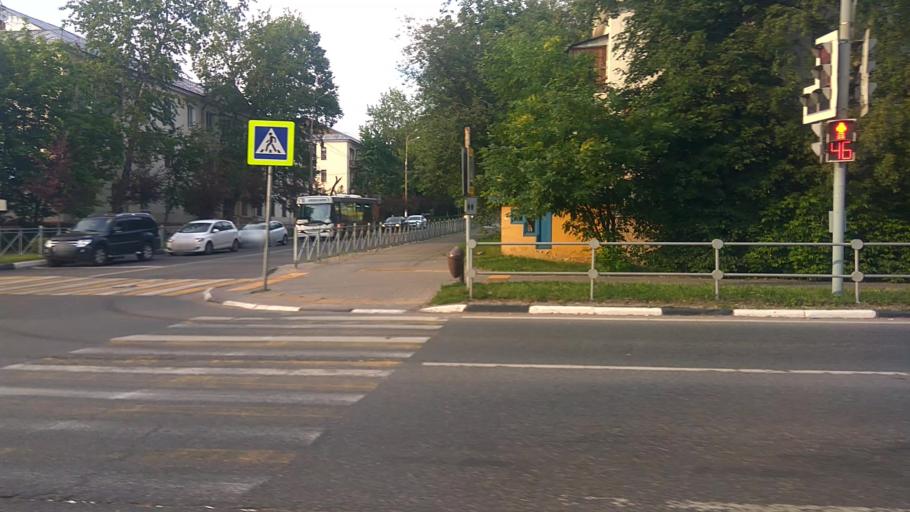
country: RU
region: Moskovskaya
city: Mytishchi
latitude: 55.9140
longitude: 37.7301
